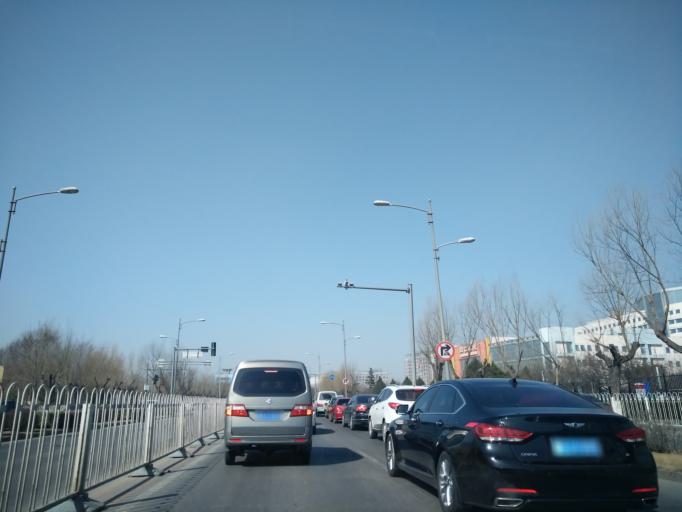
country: CN
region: Beijing
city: Jiugong
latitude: 39.7710
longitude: 116.5154
